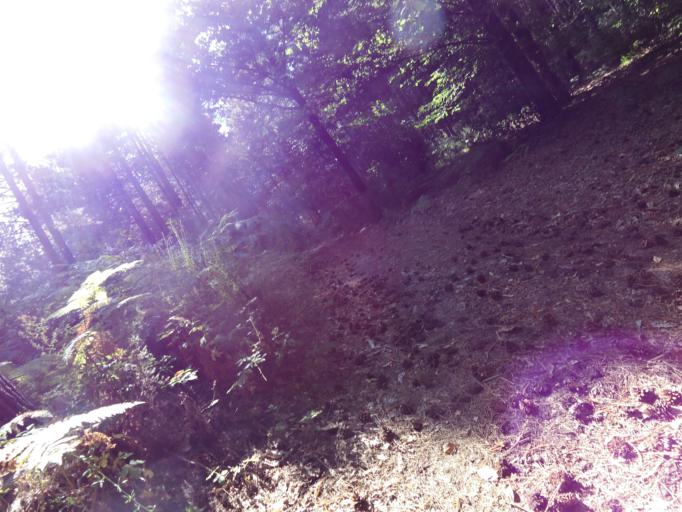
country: IT
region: Calabria
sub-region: Provincia di Vibo-Valentia
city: Nardodipace
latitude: 38.4873
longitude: 16.3826
